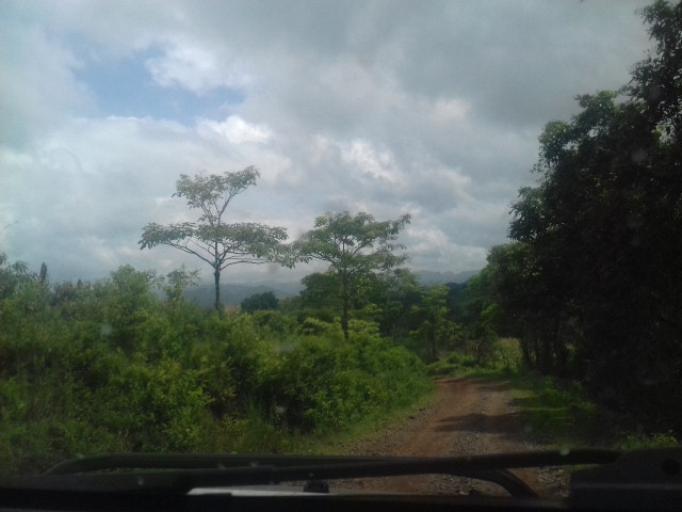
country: NI
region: Matagalpa
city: Matiguas
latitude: 12.9346
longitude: -85.3693
